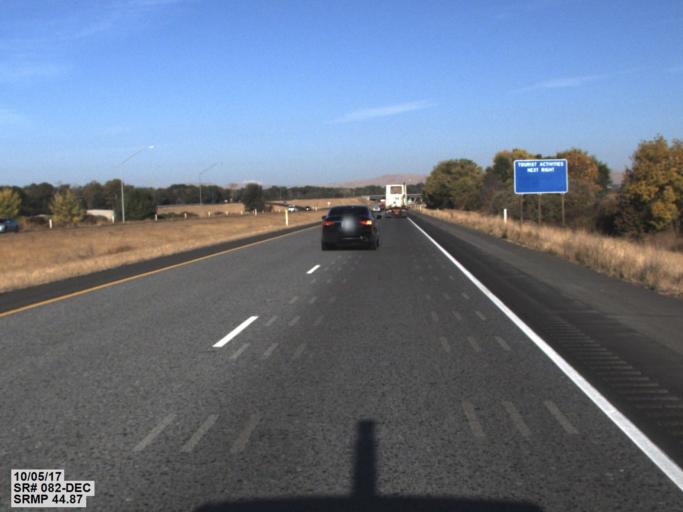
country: US
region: Washington
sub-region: Yakima County
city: Wapato
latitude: 46.4671
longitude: -120.3867
